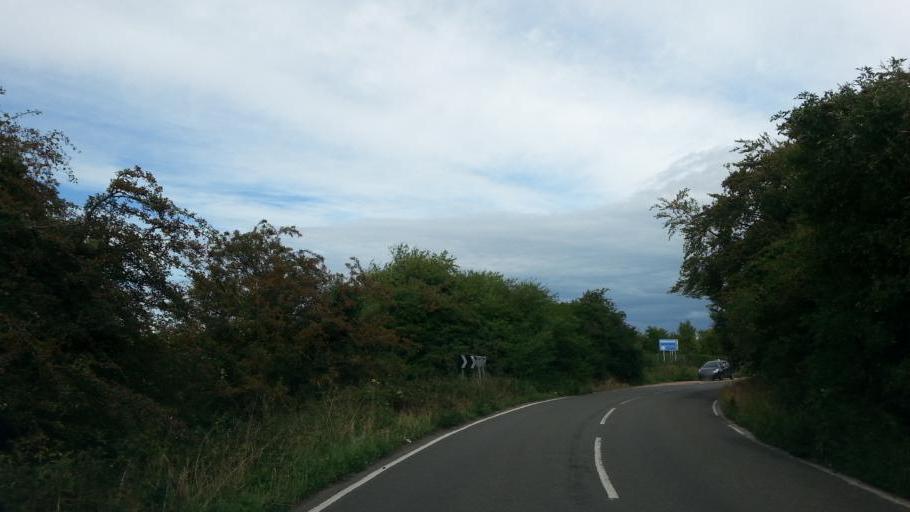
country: GB
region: England
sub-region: Cambridgeshire
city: Cambridge
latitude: 52.1769
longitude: 0.1646
